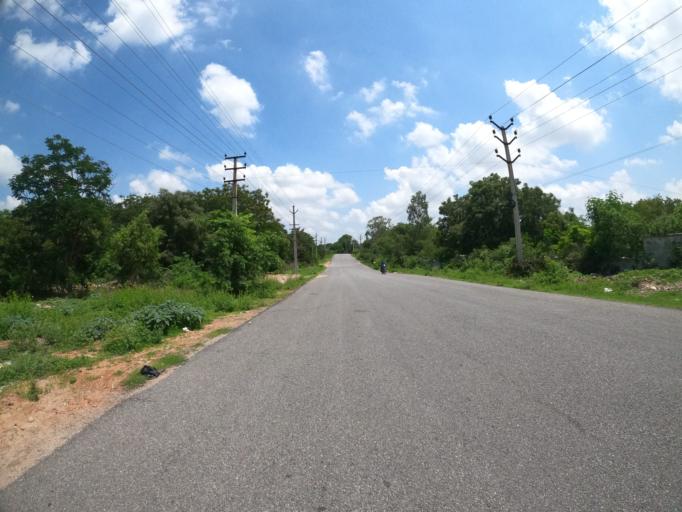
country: IN
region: Telangana
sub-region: Medak
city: Serilingampalle
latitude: 17.3924
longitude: 78.3137
